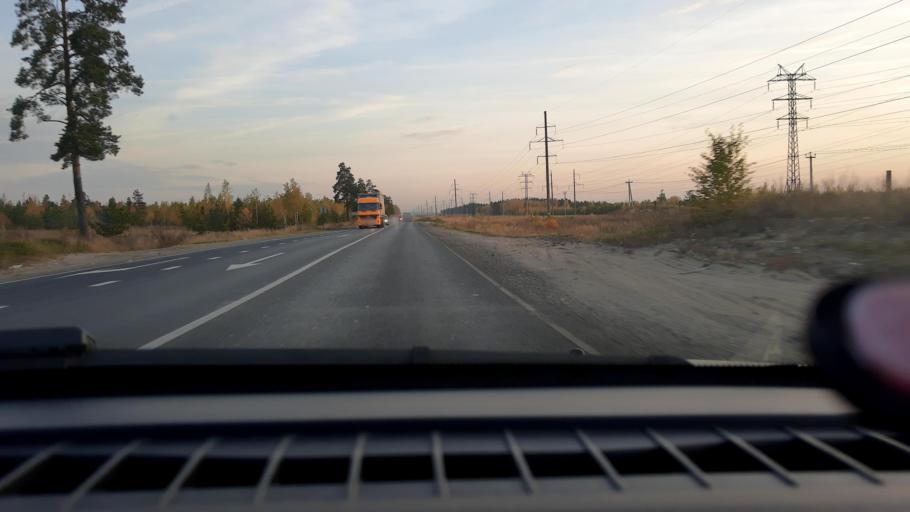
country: RU
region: Nizjnij Novgorod
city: Babino
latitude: 56.3216
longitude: 43.5590
